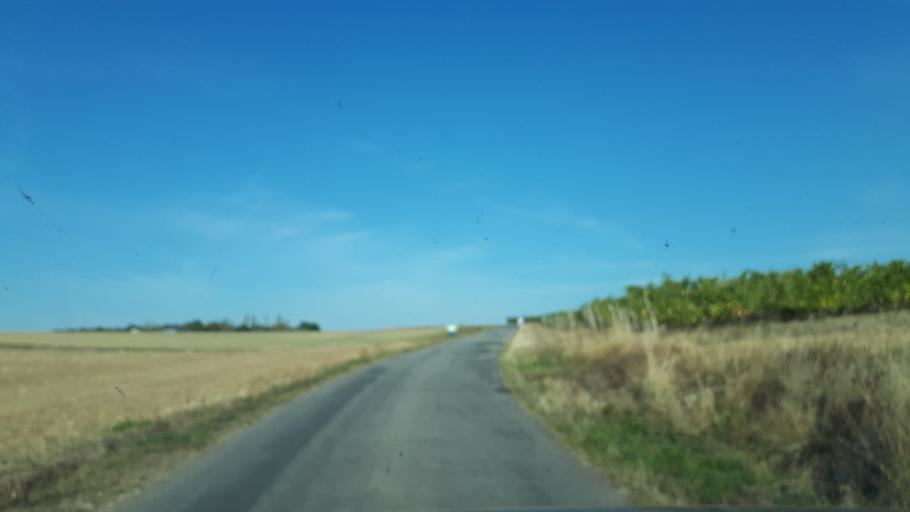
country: FR
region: Centre
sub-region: Departement du Loir-et-Cher
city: Villiers-sur-Loir
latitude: 47.8272
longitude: 0.9651
